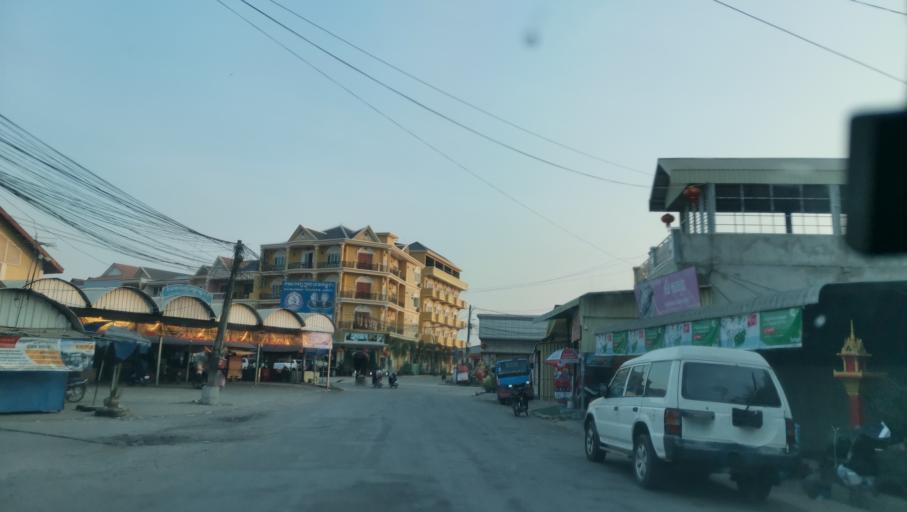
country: KH
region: Battambang
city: Battambang
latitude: 13.0855
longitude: 103.1989
